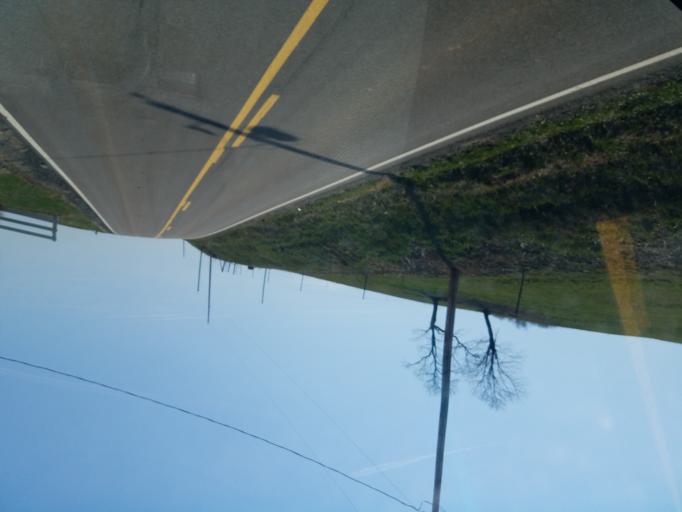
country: US
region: Ohio
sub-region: Knox County
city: Danville
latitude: 40.5278
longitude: -82.3002
